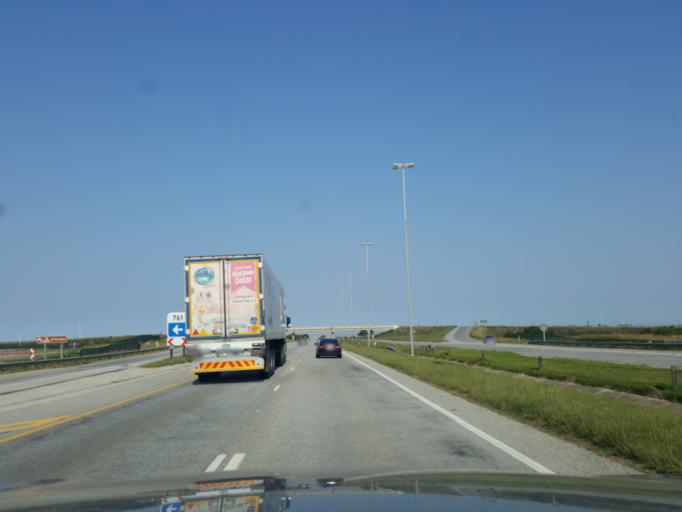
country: ZA
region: Eastern Cape
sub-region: Nelson Mandela Bay Metropolitan Municipality
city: Port Elizabeth
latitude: -33.8199
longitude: 25.6484
